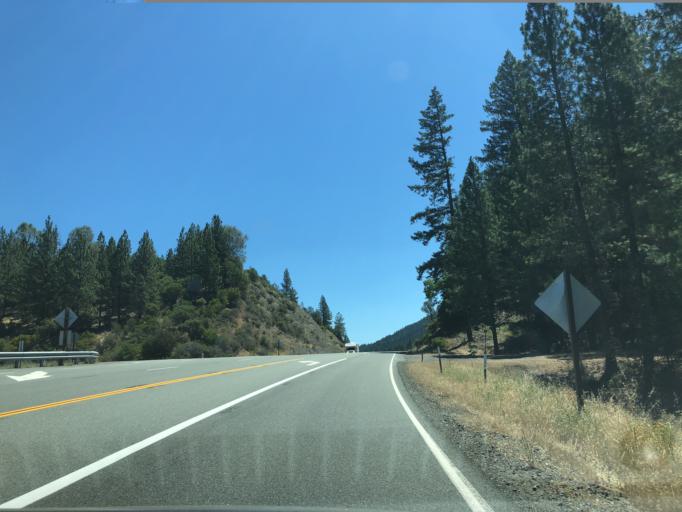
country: US
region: California
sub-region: Trinity County
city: Lewiston
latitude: 40.6730
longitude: -122.8791
